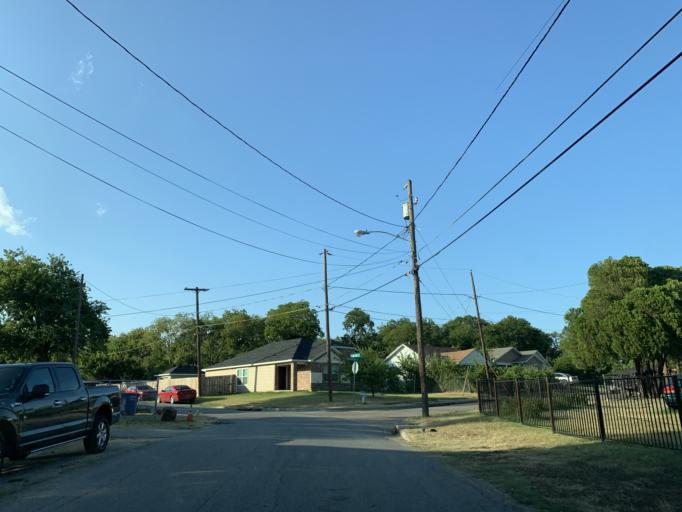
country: US
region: Texas
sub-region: Dallas County
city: Dallas
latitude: 32.6988
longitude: -96.7872
